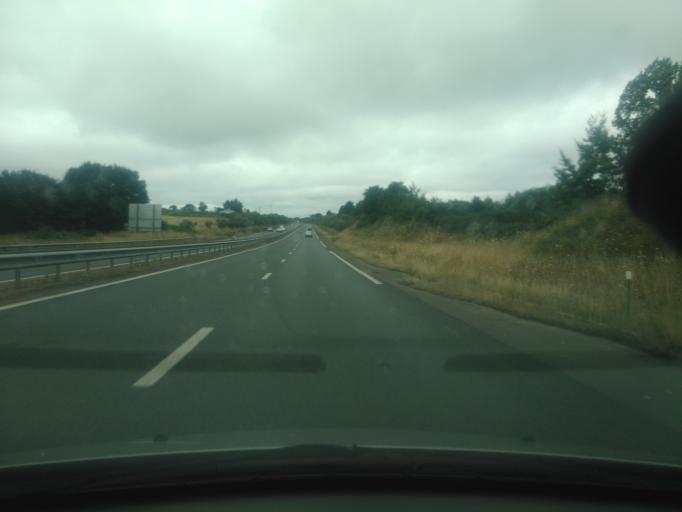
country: FR
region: Brittany
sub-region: Departement des Cotes-d'Armor
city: Jugon-les-Lacs
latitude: 48.4125
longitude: -2.3692
